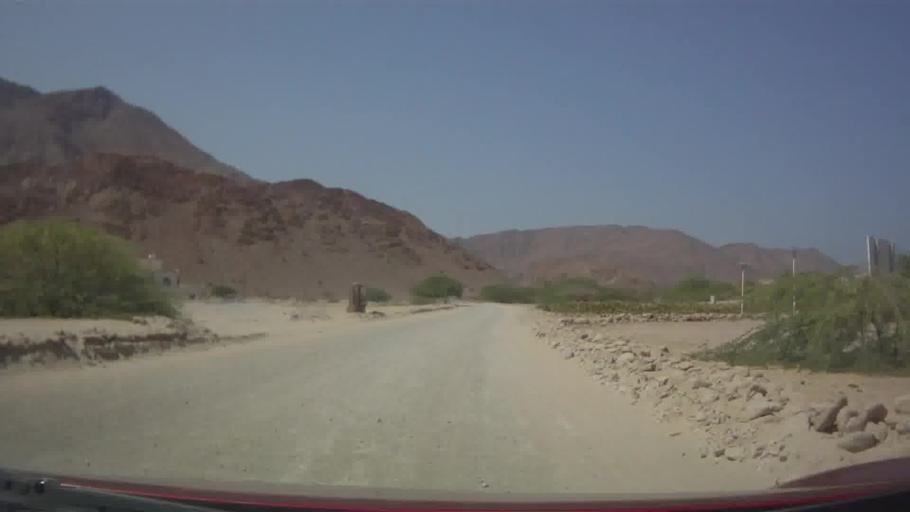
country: OM
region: Muhafazat Masqat
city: Muscat
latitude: 23.4218
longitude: 58.7838
